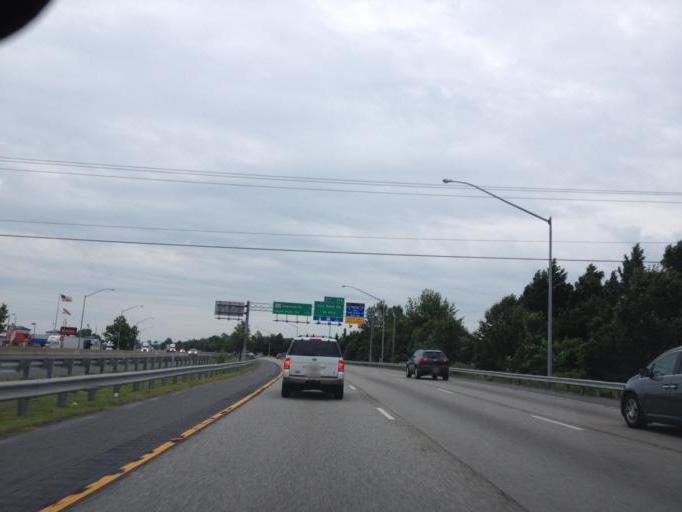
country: US
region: Maryland
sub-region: Queen Anne's County
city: Chester
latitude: 38.9746
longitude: -76.3011
